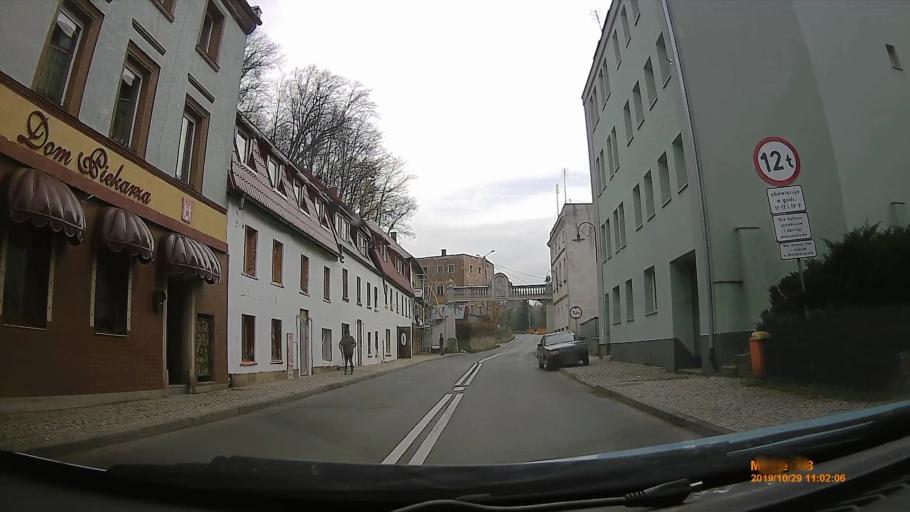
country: PL
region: Lower Silesian Voivodeship
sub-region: Powiat klodzki
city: Radkow
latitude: 50.4893
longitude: 16.4568
